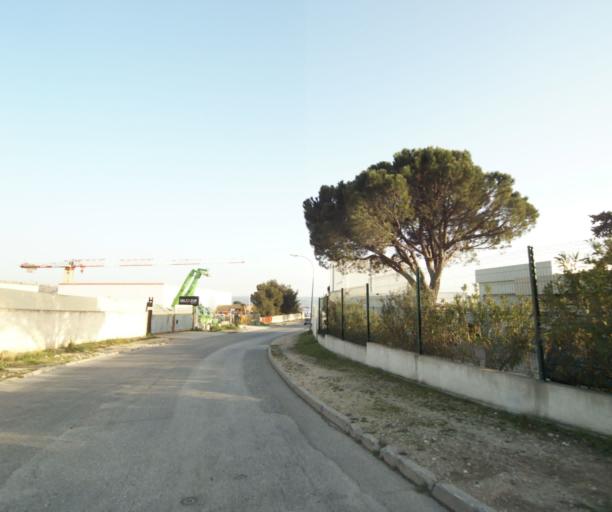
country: FR
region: Provence-Alpes-Cote d'Azur
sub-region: Departement des Bouches-du-Rhone
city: Vitrolles
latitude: 43.4365
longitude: 5.2504
